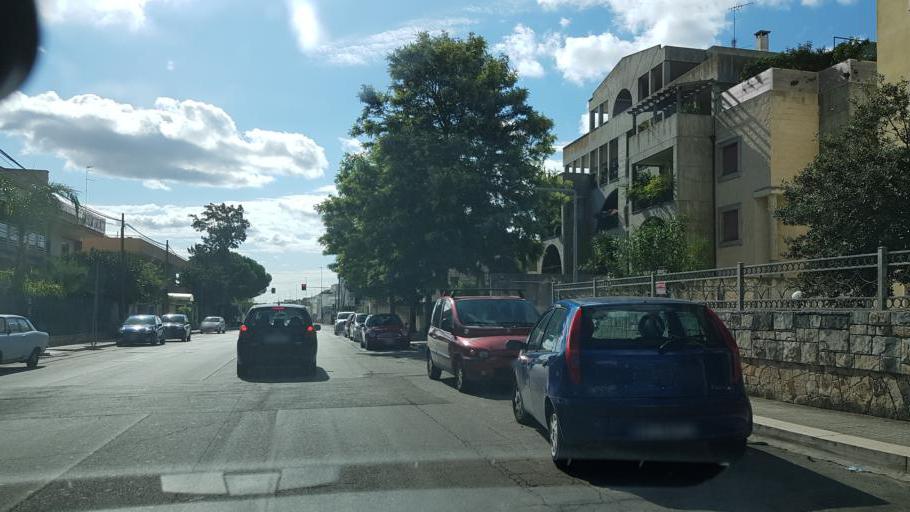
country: IT
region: Apulia
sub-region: Provincia di Lecce
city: Lecce
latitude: 40.3513
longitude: 18.1514
